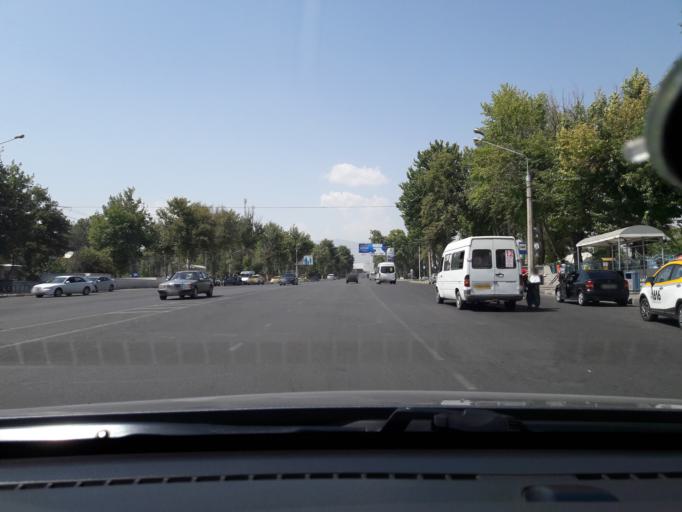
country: TJ
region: Dushanbe
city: Dushanbe
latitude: 38.5713
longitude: 68.7548
